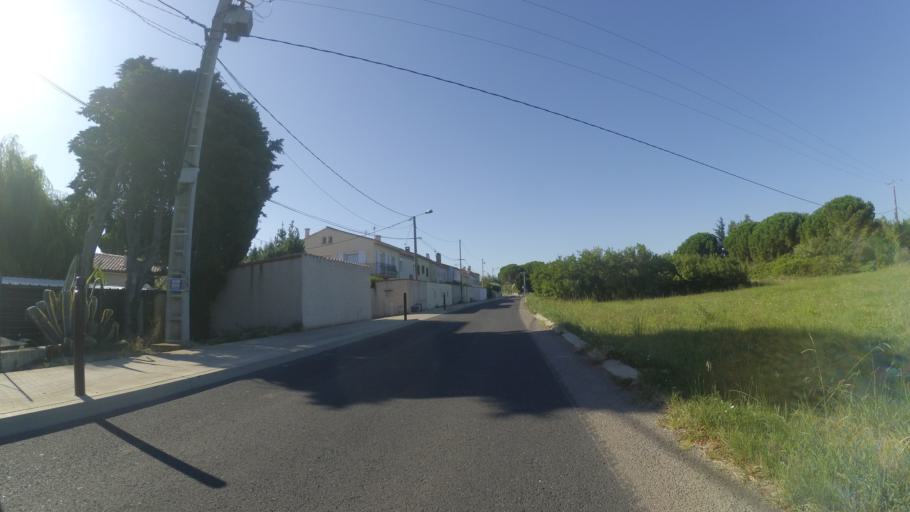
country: FR
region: Languedoc-Roussillon
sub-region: Departement des Pyrenees-Orientales
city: Villeneuve-la-Riviere
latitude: 42.6971
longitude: 2.8000
